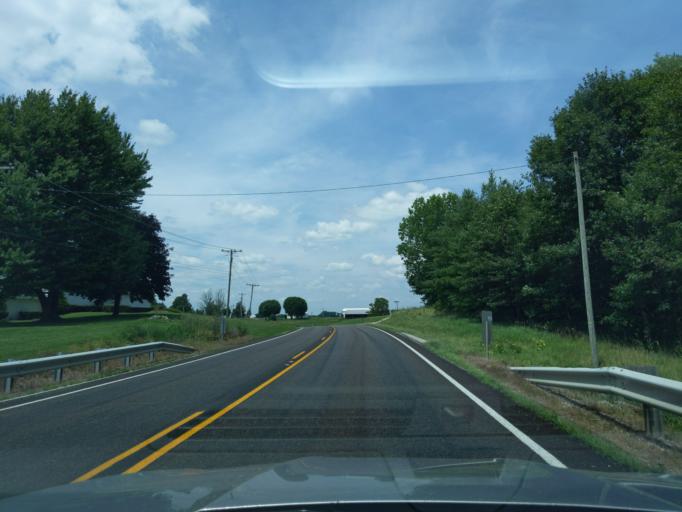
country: US
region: Indiana
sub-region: Ripley County
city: Osgood
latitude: 39.2275
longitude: -85.3367
